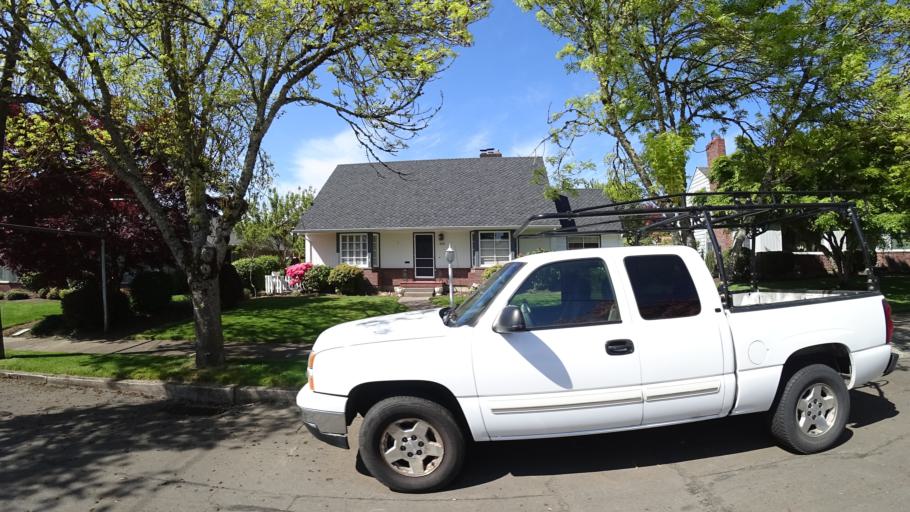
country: US
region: Oregon
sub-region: Clackamas County
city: Milwaukie
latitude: 45.4840
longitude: -122.6266
